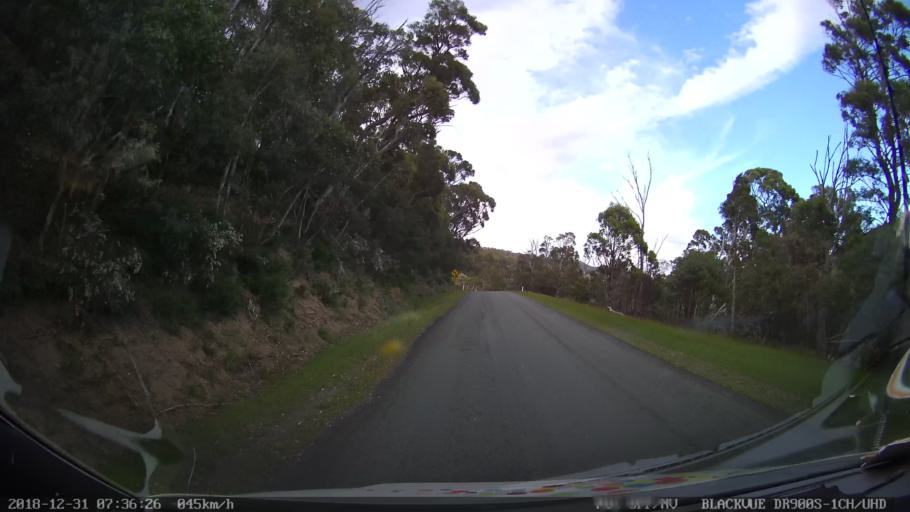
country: AU
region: New South Wales
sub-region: Snowy River
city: Jindabyne
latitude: -36.3409
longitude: 148.4427
